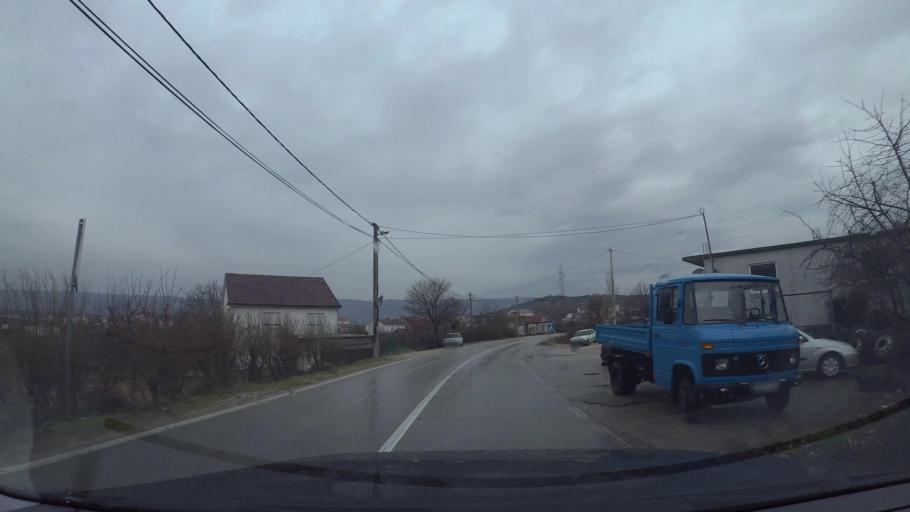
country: BA
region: Federation of Bosnia and Herzegovina
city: Blagaj
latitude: 43.2899
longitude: 17.8582
